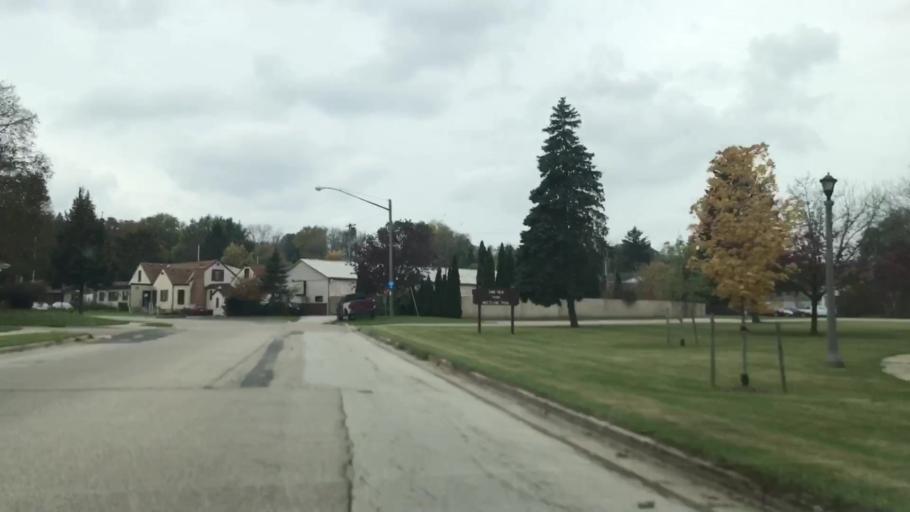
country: US
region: Wisconsin
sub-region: Waukesha County
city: Menomonee Falls
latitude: 43.1748
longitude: -88.1104
